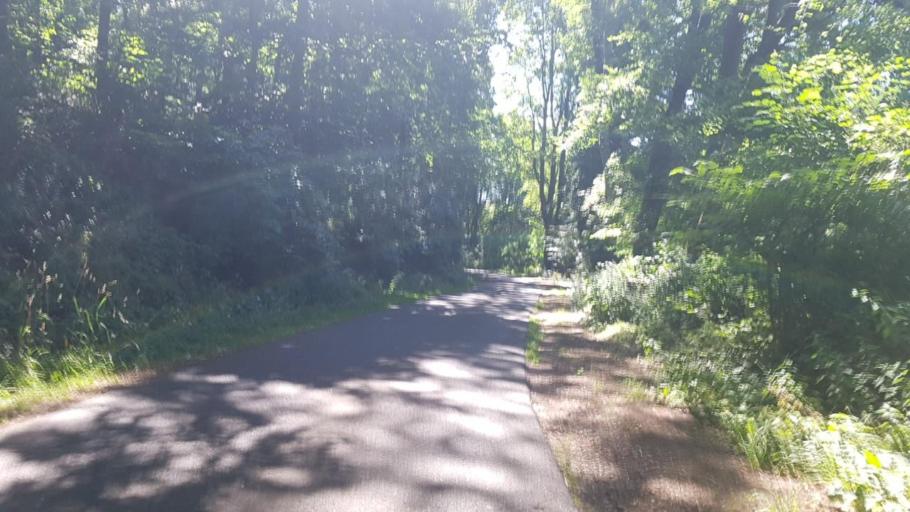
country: DE
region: North Rhine-Westphalia
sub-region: Regierungsbezirk Koln
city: Mechernich
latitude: 50.5970
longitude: 6.6238
